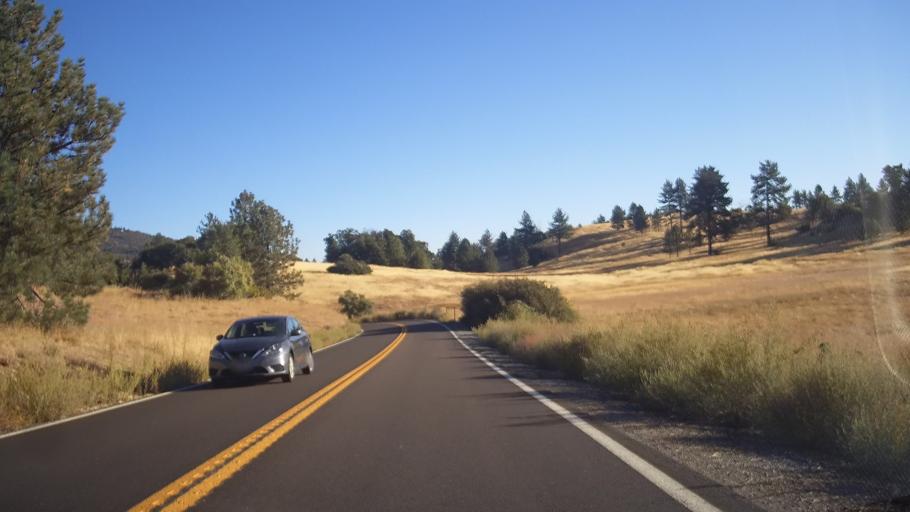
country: US
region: California
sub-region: San Diego County
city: Julian
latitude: 32.9726
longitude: -116.5770
